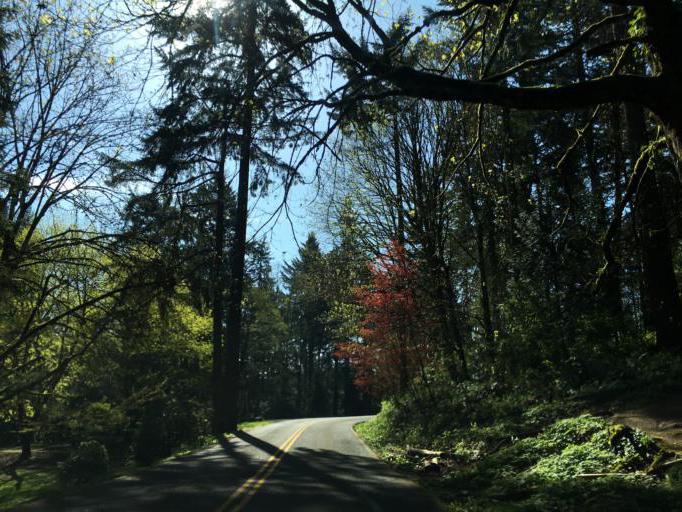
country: US
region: Oregon
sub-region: Multnomah County
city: Portland
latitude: 45.5142
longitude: -122.7057
